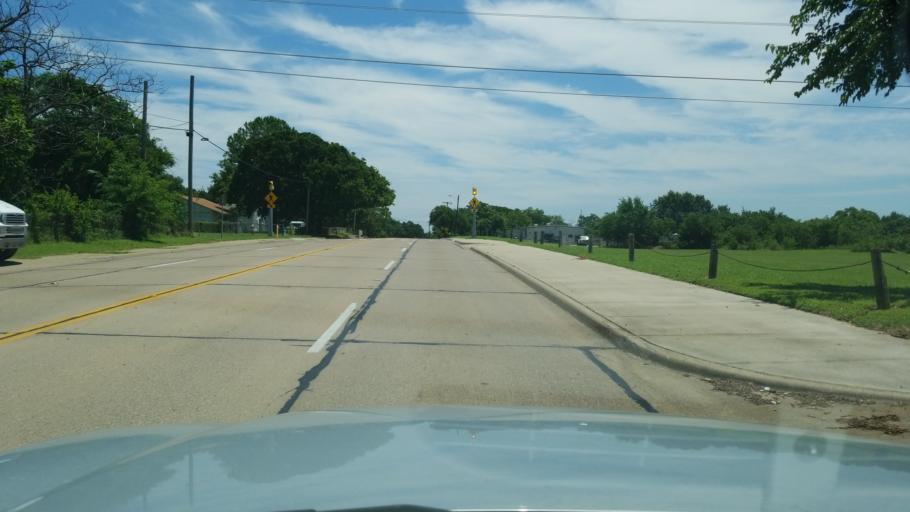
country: US
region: Texas
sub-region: Dallas County
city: Irving
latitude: 32.8012
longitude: -96.9127
